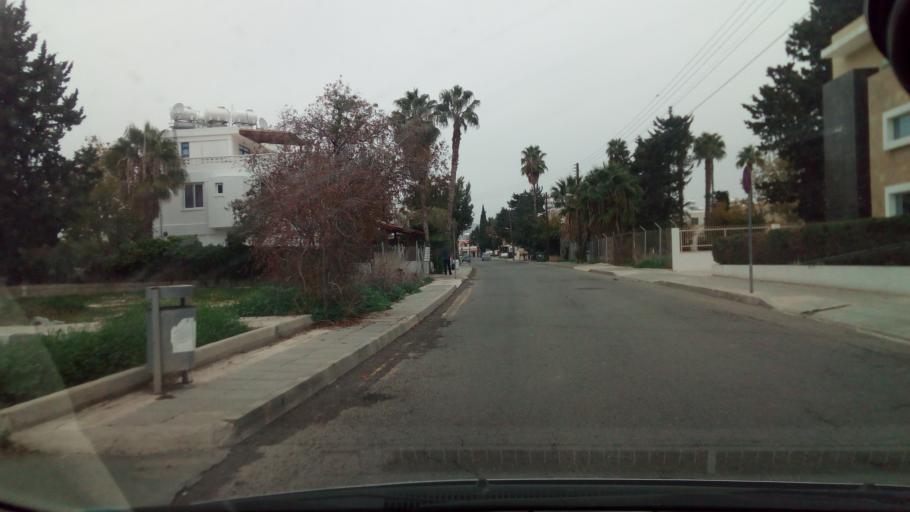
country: CY
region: Pafos
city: Paphos
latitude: 34.7561
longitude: 32.4209
